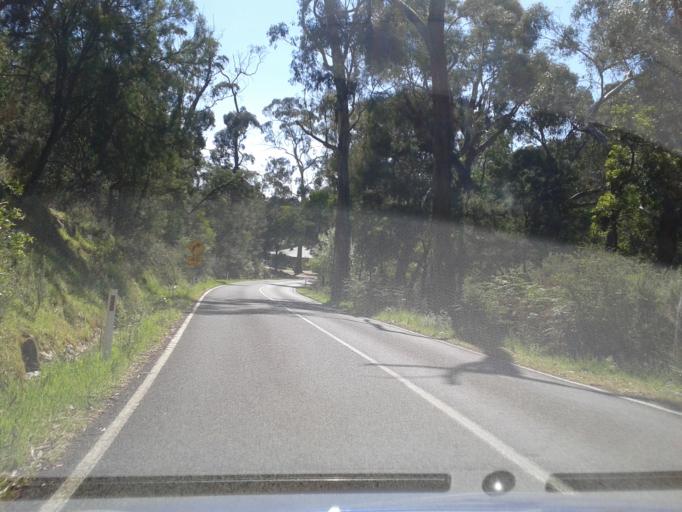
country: AU
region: Victoria
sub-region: Northern Grampians
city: Stawell
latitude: -37.1366
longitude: 142.5176
